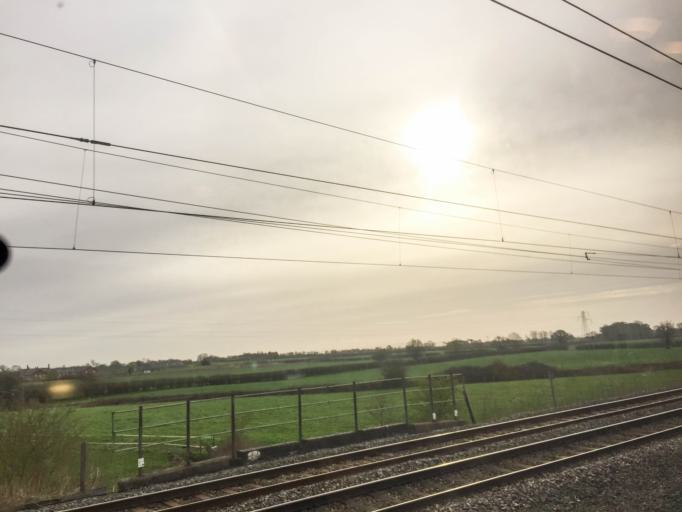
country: GB
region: England
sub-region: Cheshire West and Chester
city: Winsford
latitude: 53.1781
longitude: -2.4839
